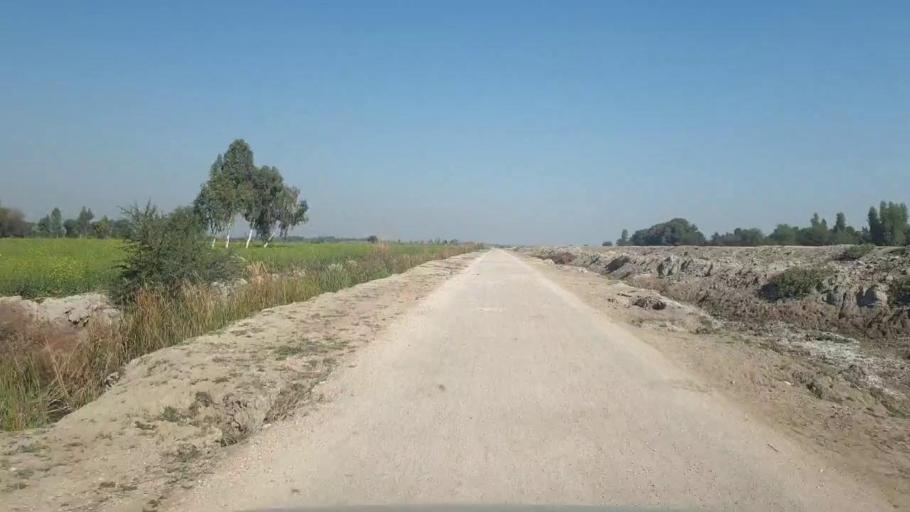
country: PK
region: Sindh
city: Mirwah Gorchani
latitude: 25.3316
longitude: 69.1020
